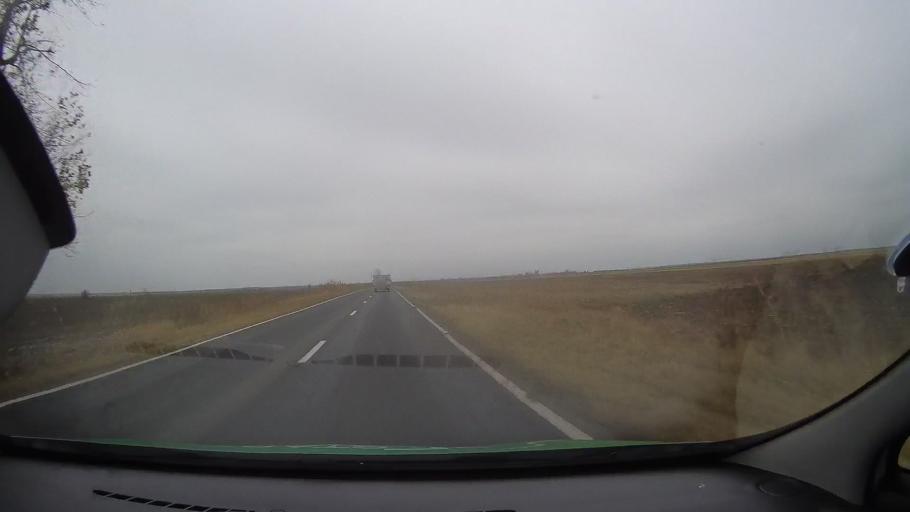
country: RO
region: Ialomita
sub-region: Comuna Scanteia
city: Scanteia
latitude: 44.7451
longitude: 27.4441
